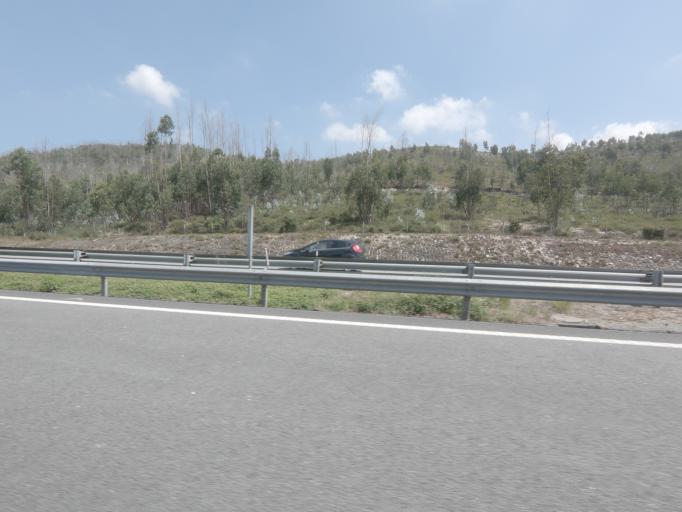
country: PT
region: Porto
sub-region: Valongo
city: Campo
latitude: 41.1908
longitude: -8.4811
